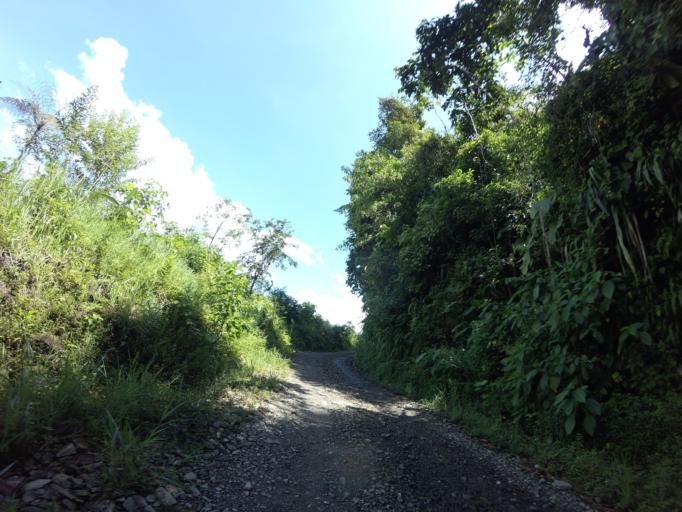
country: CO
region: Antioquia
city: Narino
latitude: 5.5156
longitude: -75.1801
